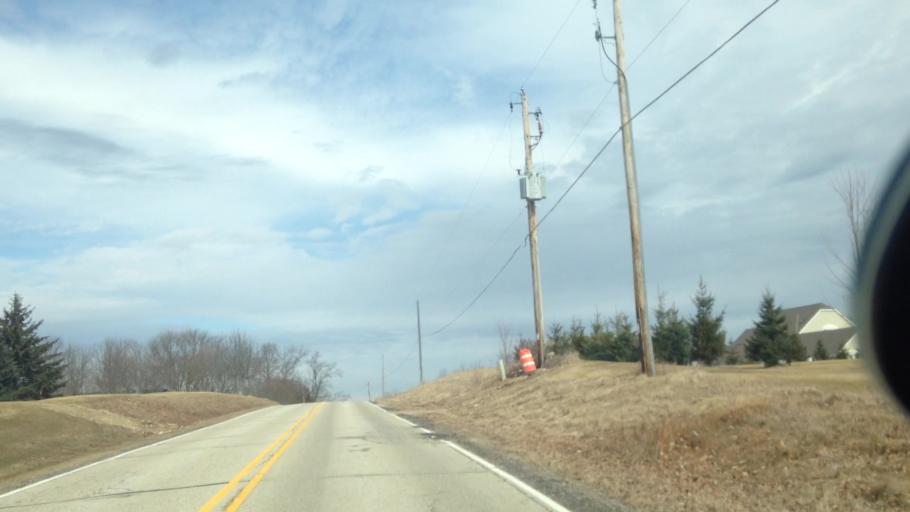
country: US
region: Wisconsin
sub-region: Waukesha County
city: Sussex
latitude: 43.1576
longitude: -88.2234
